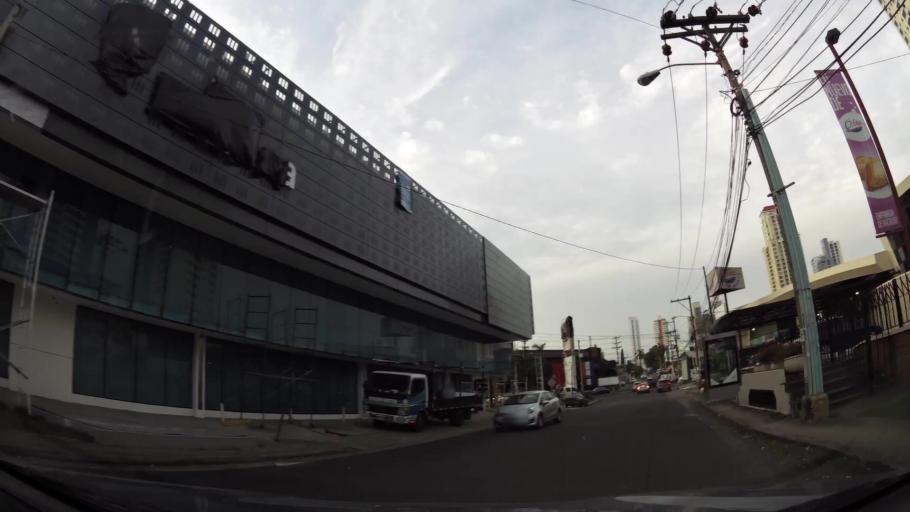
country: PA
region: Panama
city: Panama
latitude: 8.9881
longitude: -79.5120
